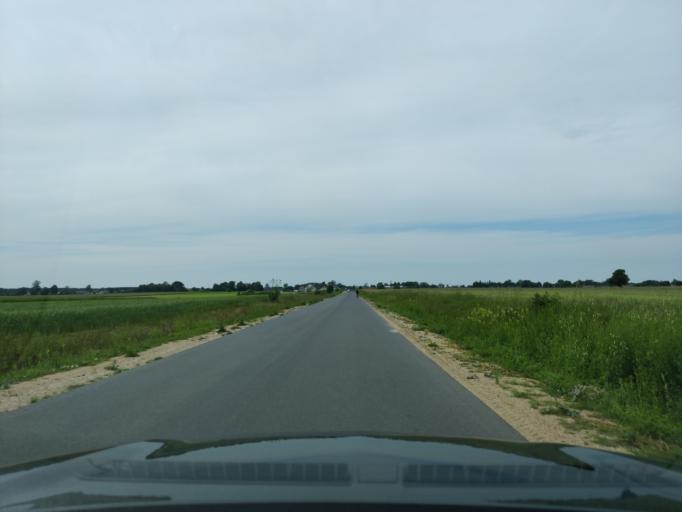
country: PL
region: Masovian Voivodeship
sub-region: Powiat pultuski
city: Obryte
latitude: 52.7191
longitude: 21.2769
